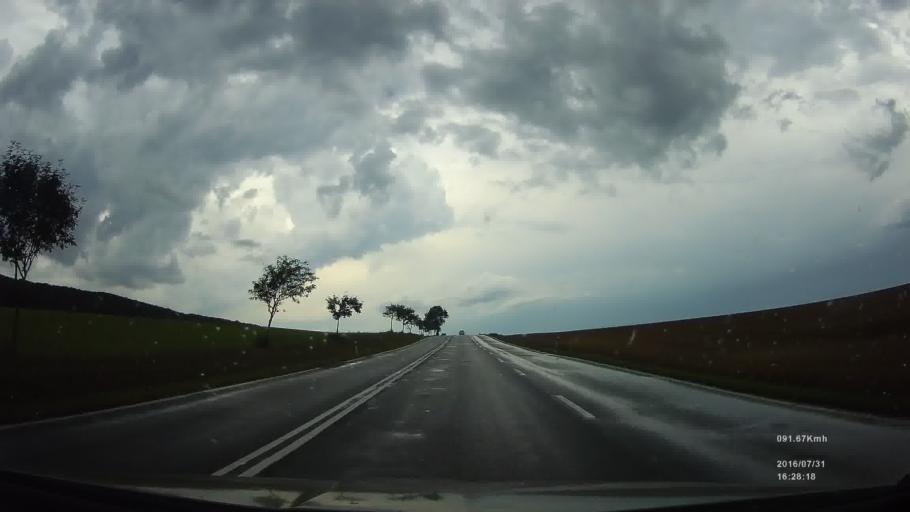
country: SK
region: Presovsky
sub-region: Okres Bardejov
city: Bardejov
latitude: 49.2307
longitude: 21.2852
